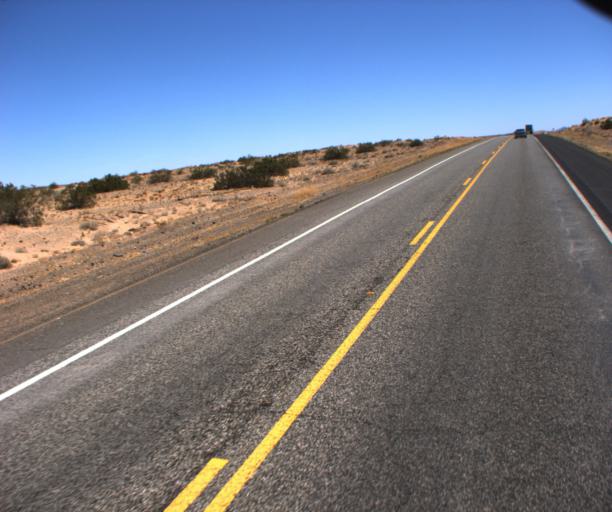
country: US
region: Arizona
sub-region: La Paz County
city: Parker
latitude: 34.0731
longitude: -114.2617
